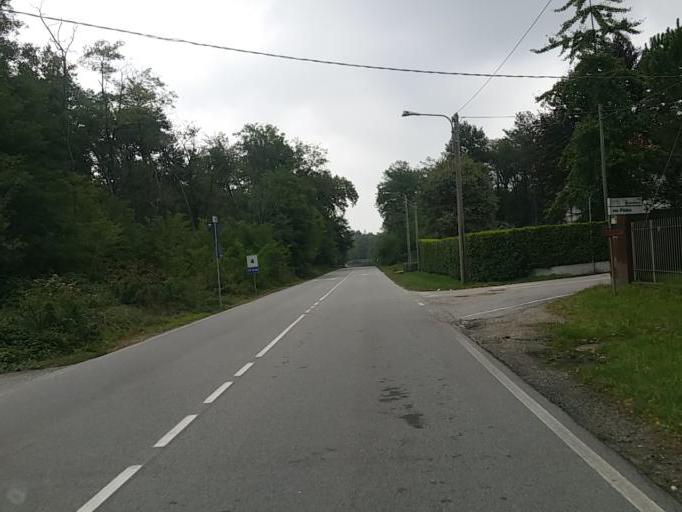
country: IT
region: Piedmont
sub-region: Provincia di Novara
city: Gattico
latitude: 45.7096
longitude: 8.5398
